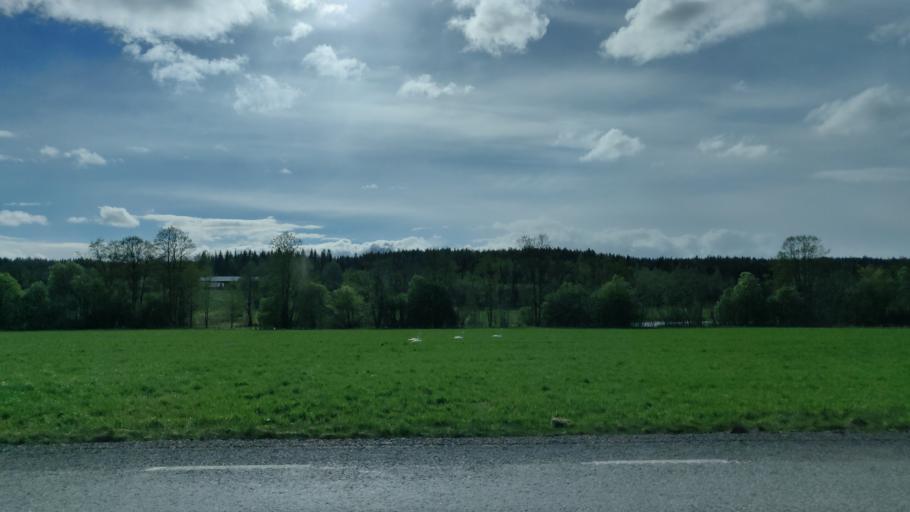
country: SE
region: Vaermland
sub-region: Forshaga Kommun
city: Forshaga
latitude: 59.5621
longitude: 13.4816
